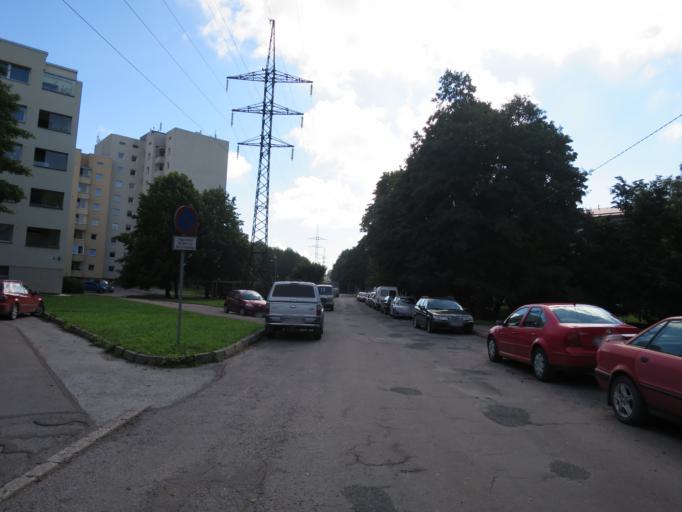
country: EE
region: Harju
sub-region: Tallinna linn
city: Tallinn
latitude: 59.4048
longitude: 24.7084
